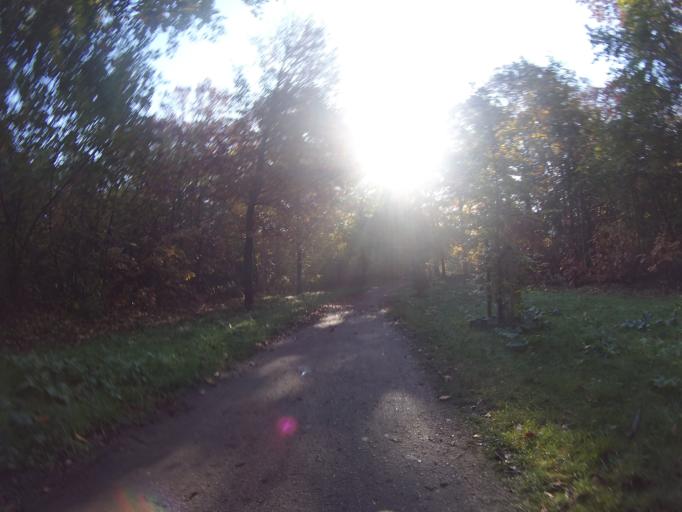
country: NL
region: Utrecht
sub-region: Gemeente Amersfoort
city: Amersfoort
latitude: 52.1360
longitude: 5.3832
